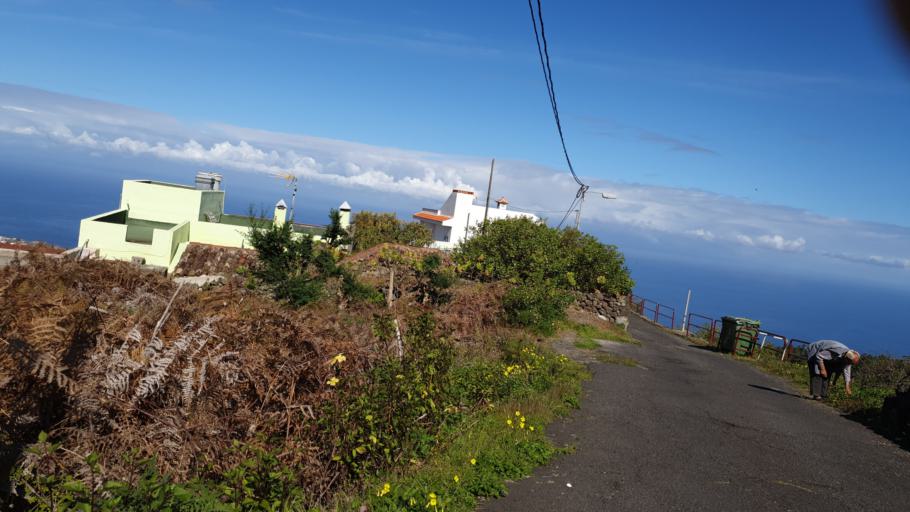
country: ES
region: Canary Islands
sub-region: Provincia de Santa Cruz de Tenerife
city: La Guancha
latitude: 28.3567
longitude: -16.6837
